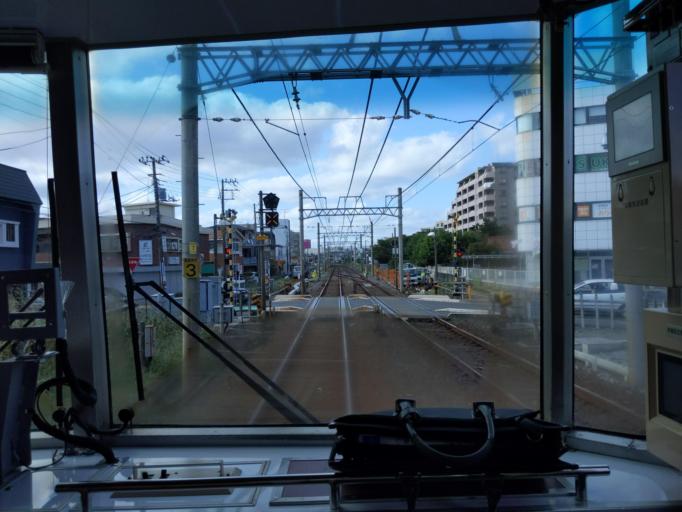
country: JP
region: Chiba
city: Funabashi
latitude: 35.7228
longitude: 140.0404
